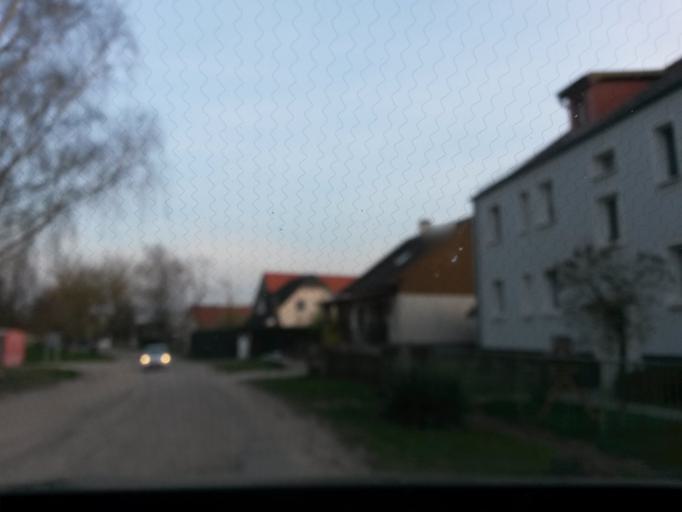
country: DE
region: Brandenburg
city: Protzel
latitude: 52.5681
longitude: 13.9680
